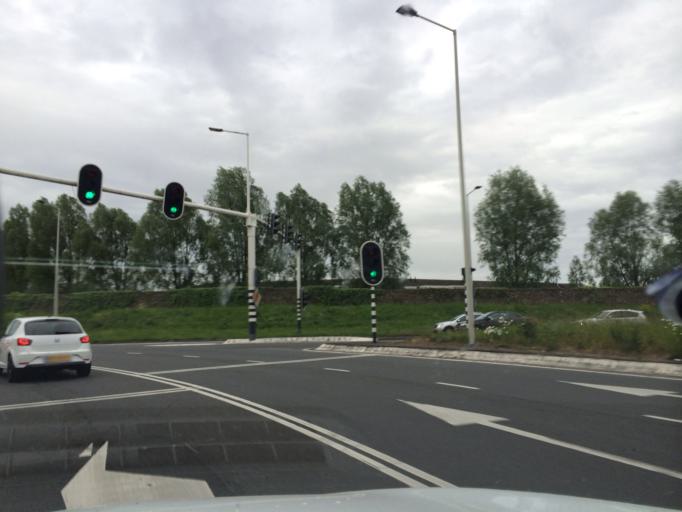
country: NL
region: South Holland
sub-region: Gemeente Capelle aan den IJssel
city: Capelle-West
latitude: 51.9249
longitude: 4.5679
